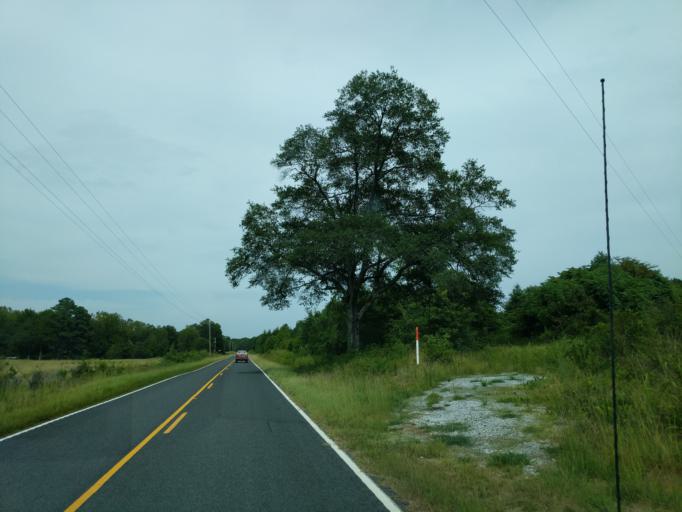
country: US
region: South Carolina
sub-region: Abbeville County
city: Lake Secession
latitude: 34.2227
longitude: -82.5817
